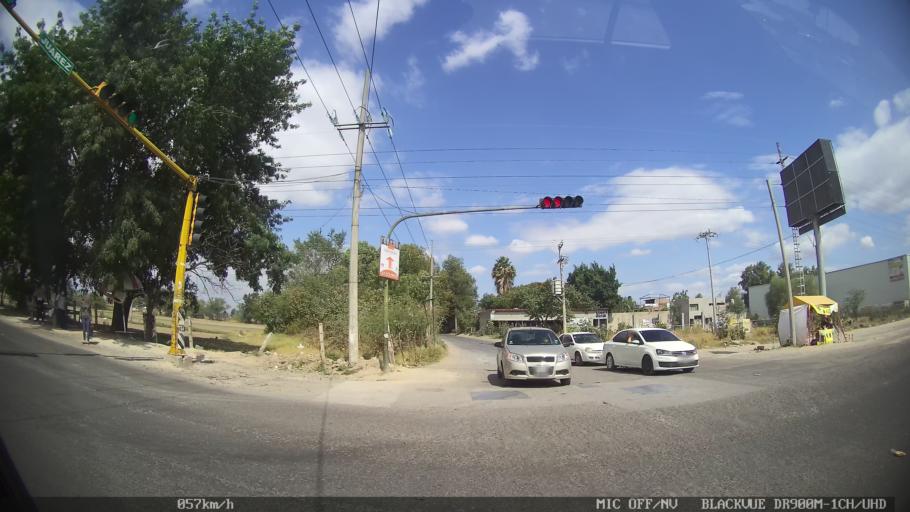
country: MX
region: Jalisco
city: Tonala
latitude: 20.6539
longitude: -103.2345
